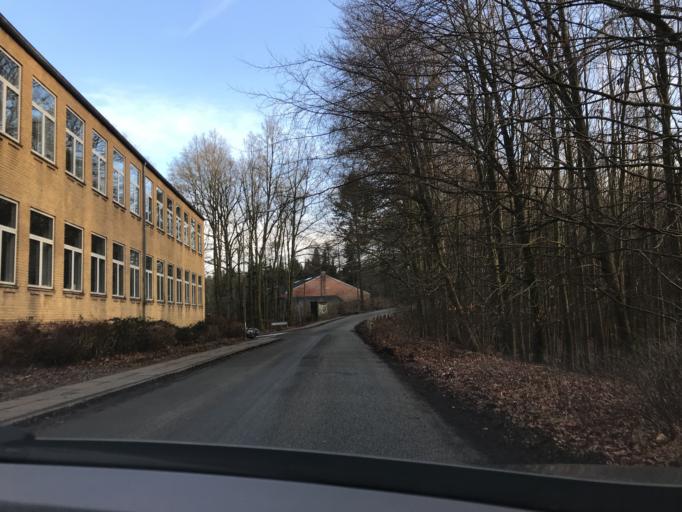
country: DK
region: South Denmark
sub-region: Vejle Kommune
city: Vejle
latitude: 55.6921
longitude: 9.5294
